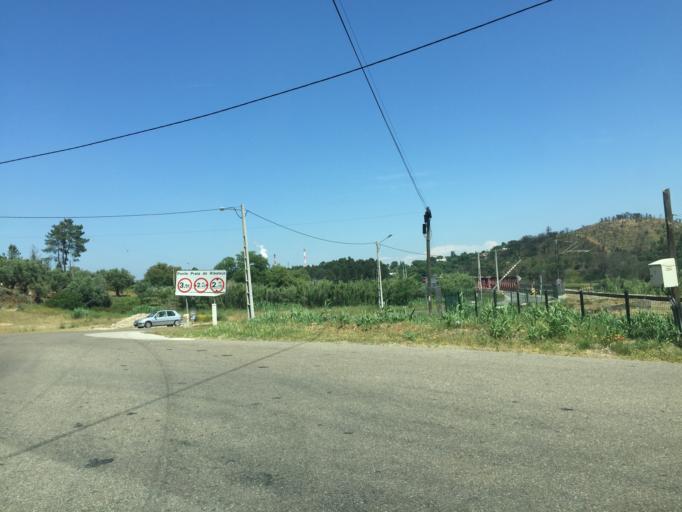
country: PT
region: Santarem
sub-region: Constancia
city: Constancia
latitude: 39.4685
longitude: -8.3448
